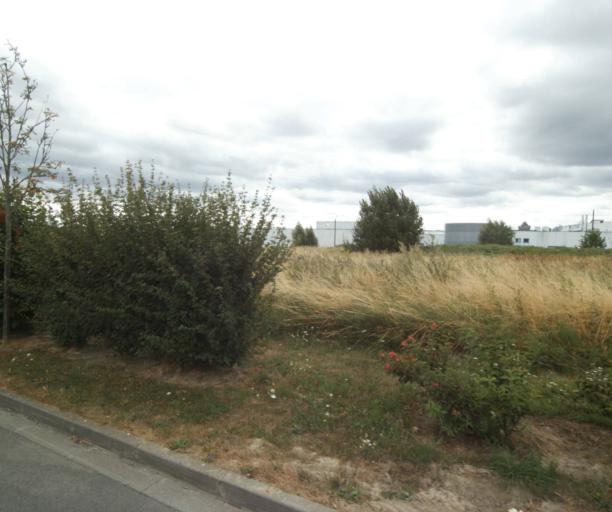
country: FR
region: Nord-Pas-de-Calais
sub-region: Departement du Nord
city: Linselles
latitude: 50.7501
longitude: 3.0827
